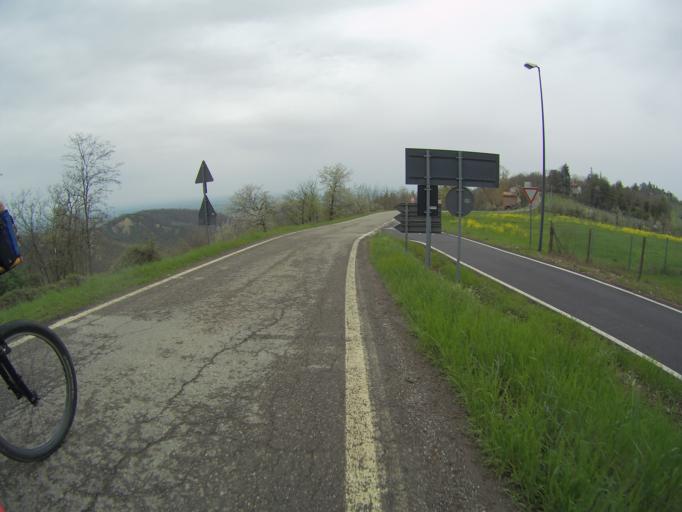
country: IT
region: Emilia-Romagna
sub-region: Provincia di Reggio Emilia
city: Quattro Castella
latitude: 44.6157
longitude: 10.4609
